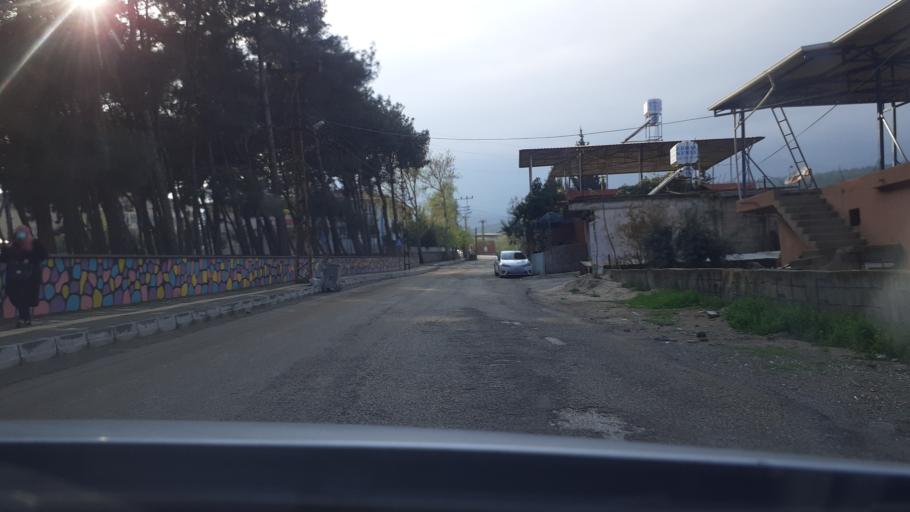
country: TR
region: Hatay
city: Kirikhan
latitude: 36.4997
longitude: 36.3392
